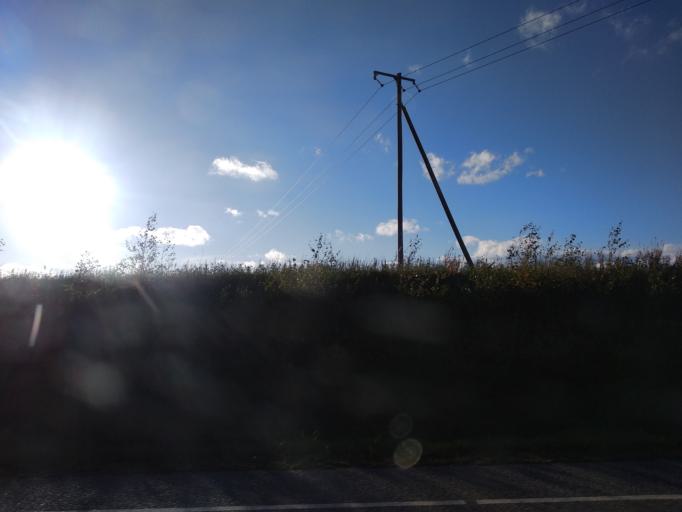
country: EE
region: Polvamaa
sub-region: Polva linn
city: Polva
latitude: 58.0385
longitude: 27.0659
